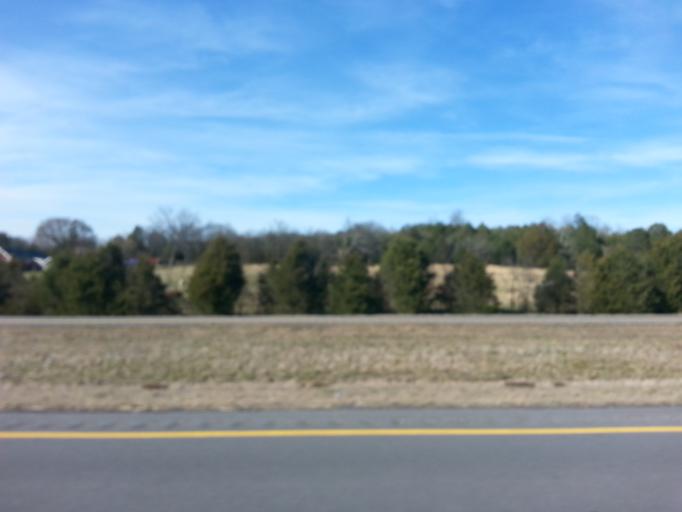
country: US
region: Tennessee
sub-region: Cannon County
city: Woodbury
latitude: 35.8050
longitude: -86.1383
